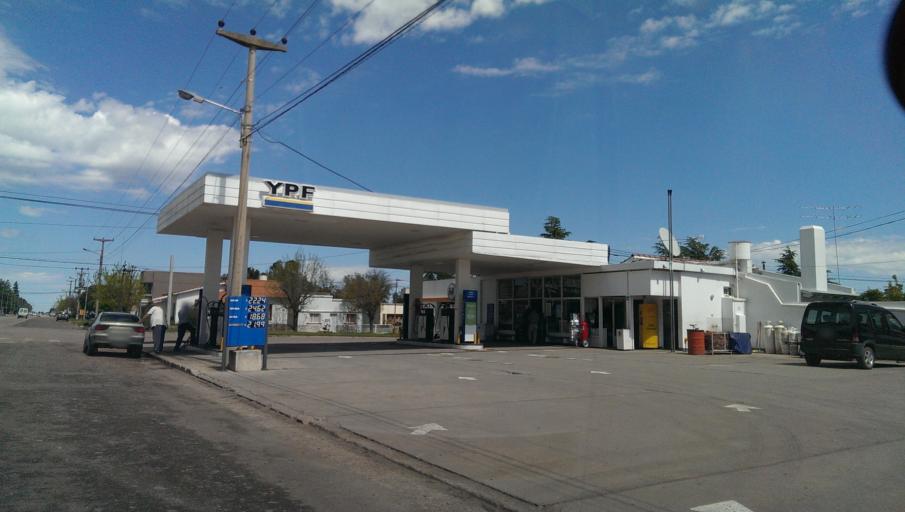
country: AR
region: Buenos Aires
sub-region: Partido de Tornquist
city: Tornquist
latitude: -38.0992
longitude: -62.2181
